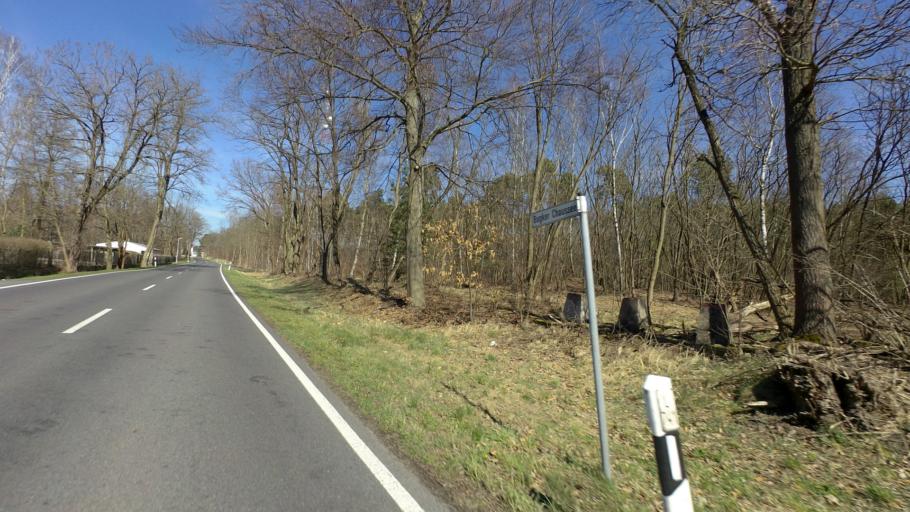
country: DE
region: Brandenburg
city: Storkow
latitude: 52.2315
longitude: 13.9471
